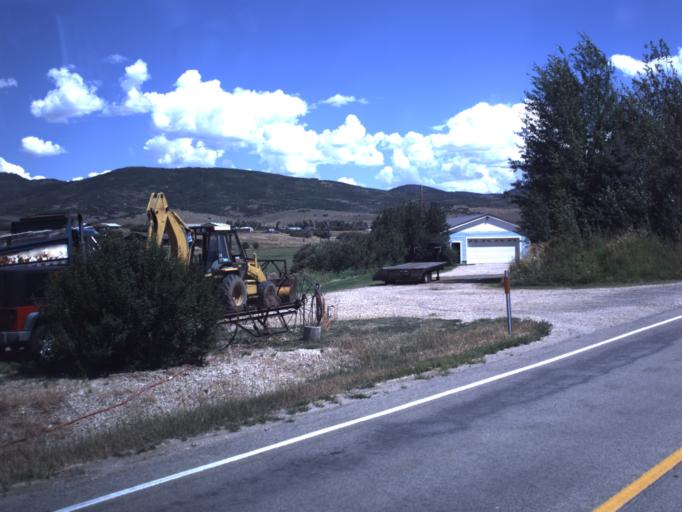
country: US
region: Utah
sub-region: Summit County
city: Oakley
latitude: 40.7238
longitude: -111.3145
